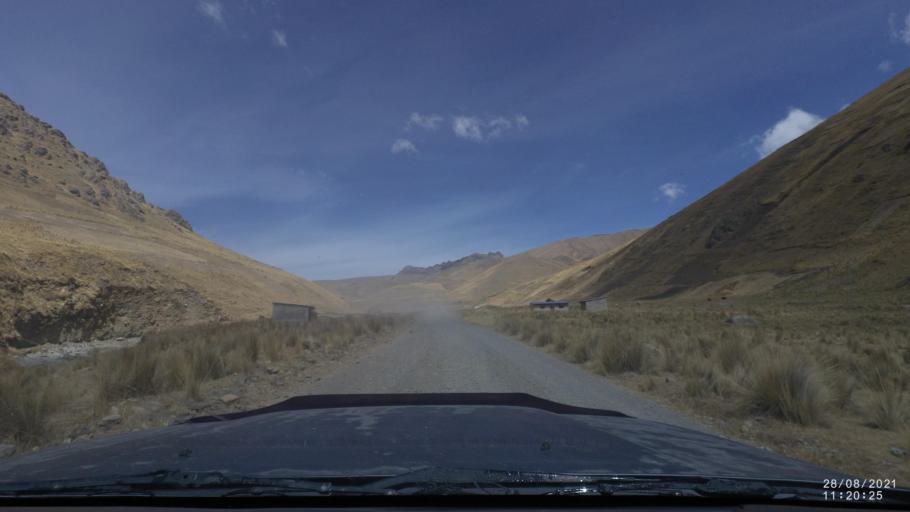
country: BO
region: Cochabamba
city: Sipe Sipe
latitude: -17.1584
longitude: -66.3403
